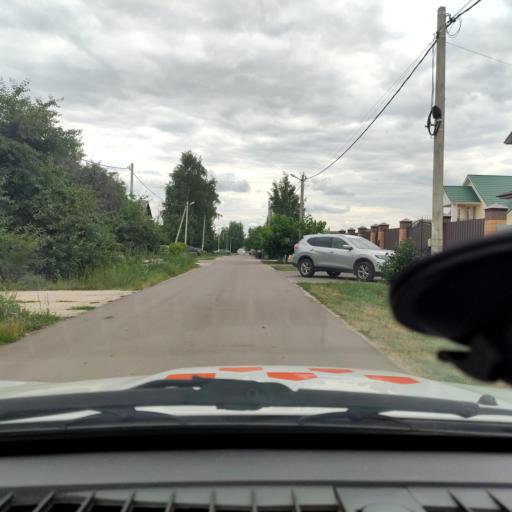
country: RU
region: Voronezj
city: Ramon'
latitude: 51.8280
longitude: 39.2588
